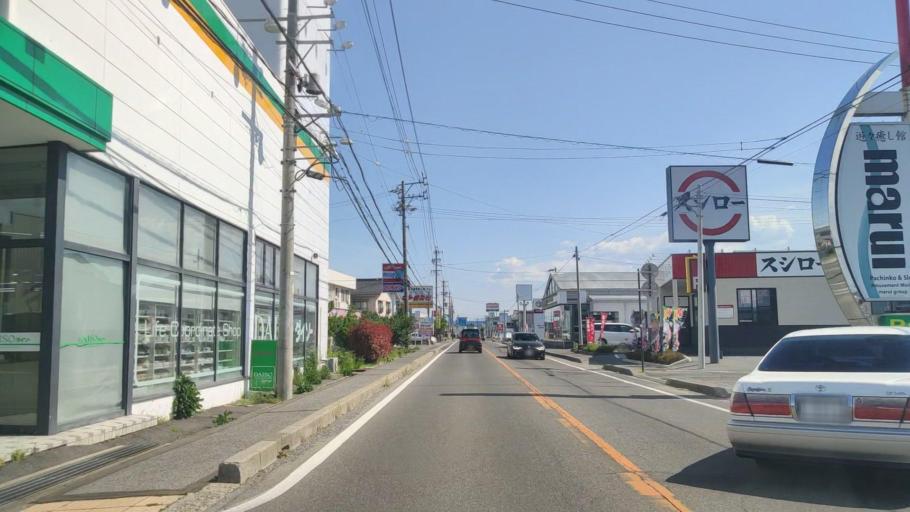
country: JP
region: Nagano
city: Hotaka
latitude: 36.3273
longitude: 137.8926
